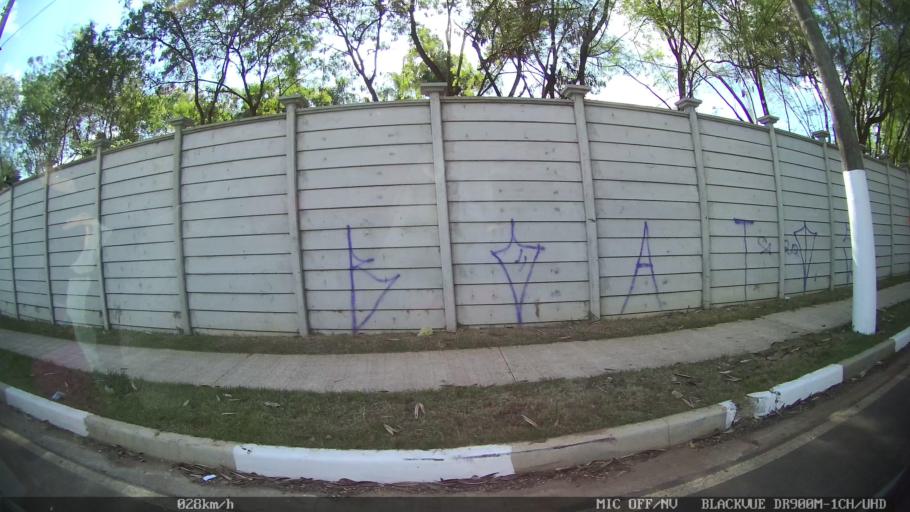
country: BR
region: Sao Paulo
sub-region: Hortolandia
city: Hortolandia
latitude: -22.8878
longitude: -47.2080
